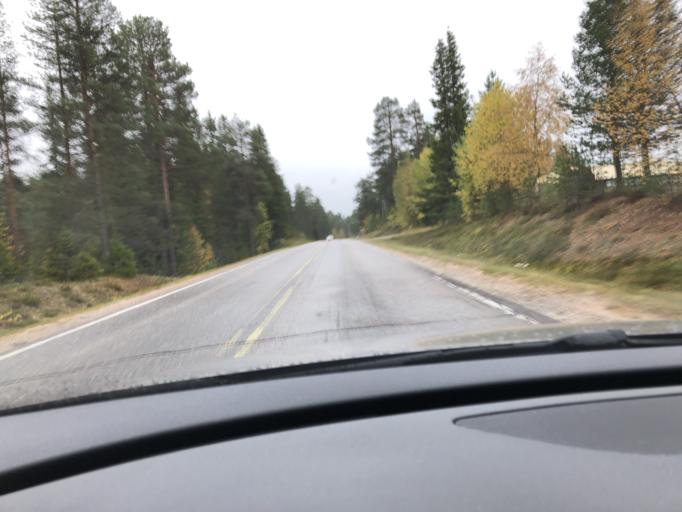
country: FI
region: Lapland
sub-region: Itae-Lappi
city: Posio
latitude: 66.1175
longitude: 28.1824
